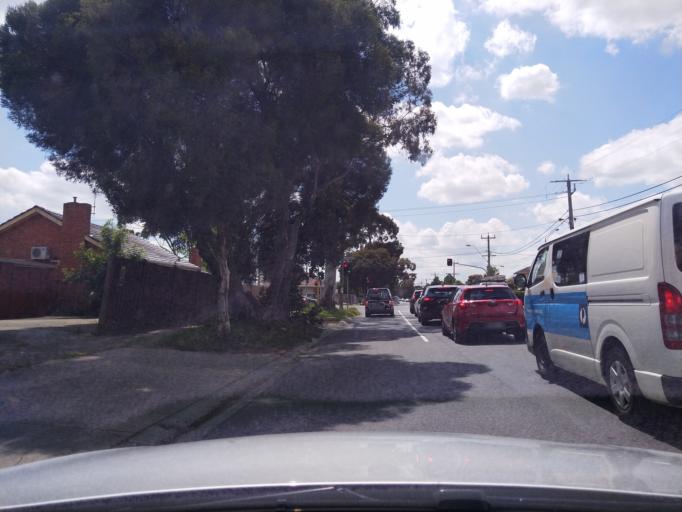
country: AU
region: Victoria
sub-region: Banyule
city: Heidelberg Heights
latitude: -37.7427
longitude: 145.0477
